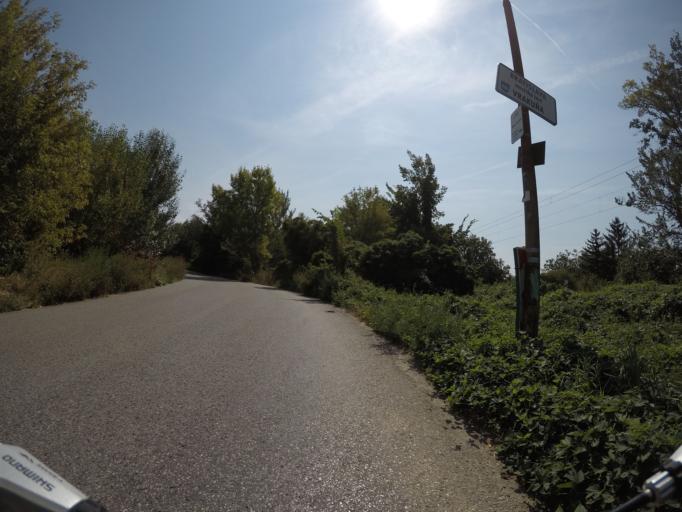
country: SK
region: Bratislavsky
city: Bratislava
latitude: 48.1536
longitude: 17.1873
